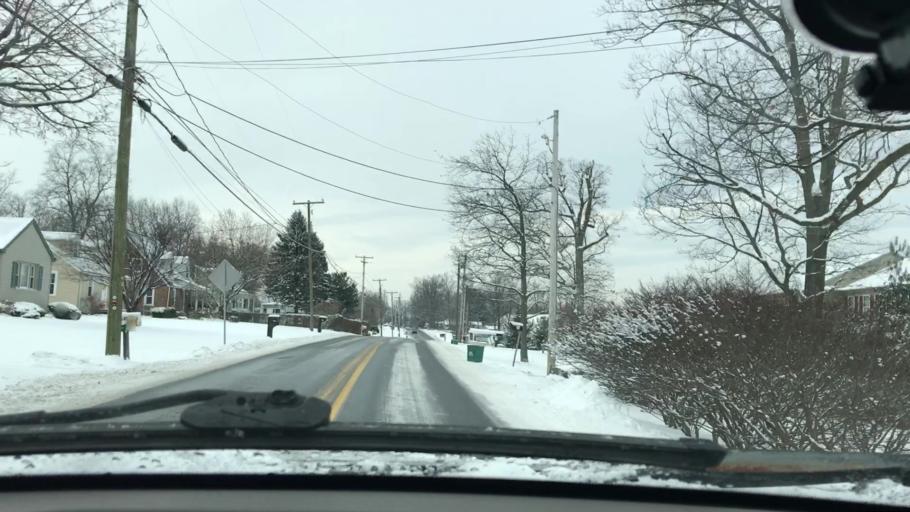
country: US
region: Pennsylvania
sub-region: Lancaster County
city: Elizabethtown
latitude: 40.1732
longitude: -76.5973
